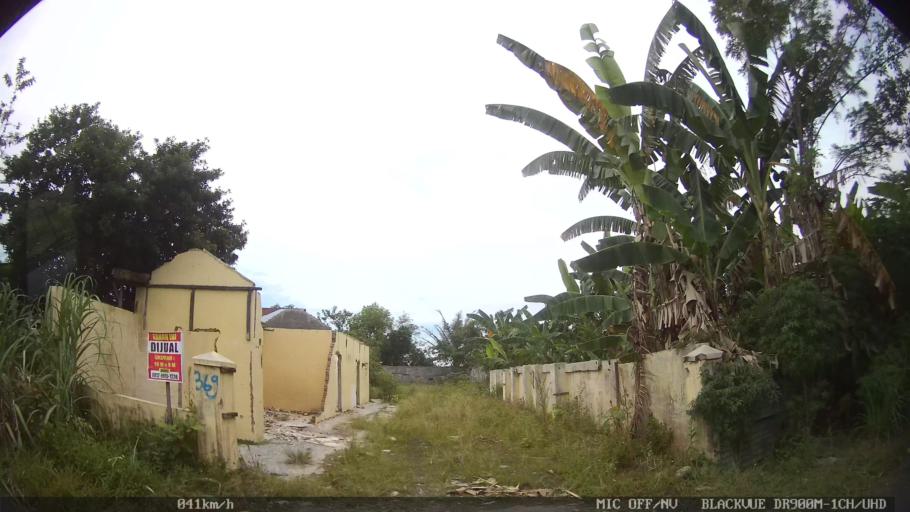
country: ID
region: North Sumatra
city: Sunggal
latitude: 3.6193
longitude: 98.5949
